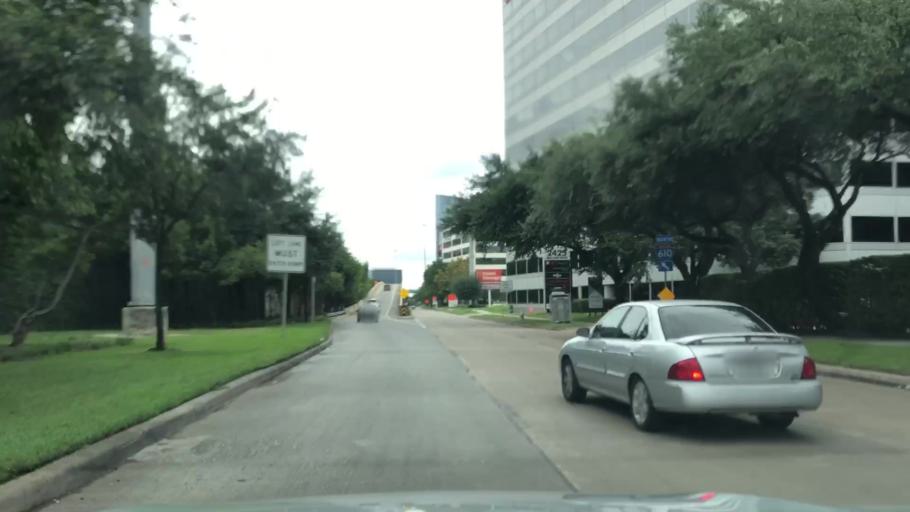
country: US
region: Texas
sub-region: Harris County
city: West University Place
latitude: 29.7415
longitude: -95.4577
